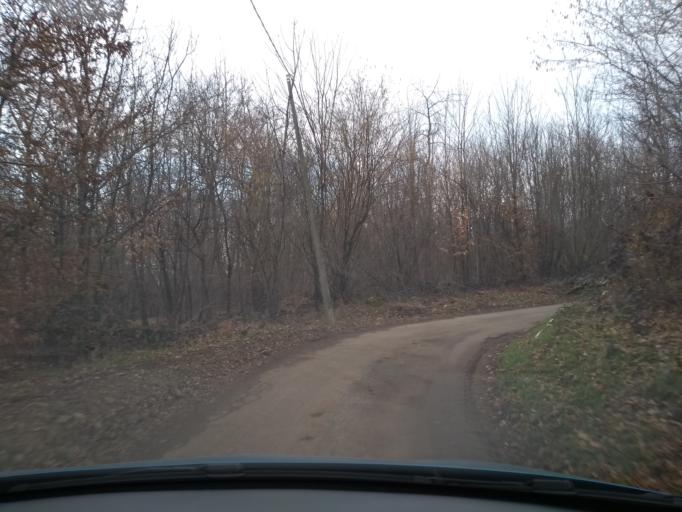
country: IT
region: Piedmont
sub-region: Provincia di Torino
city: Mathi
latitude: 45.2696
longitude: 7.5408
